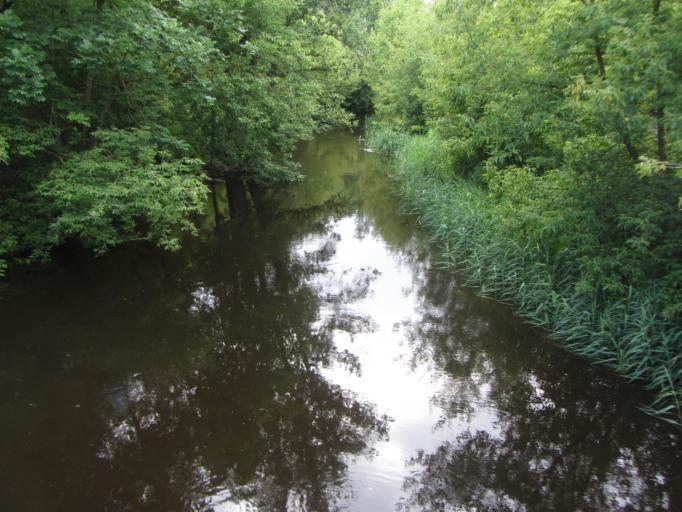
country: LT
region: Panevezys
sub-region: Panevezys City
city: Panevezys
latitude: 55.7524
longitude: 24.2460
